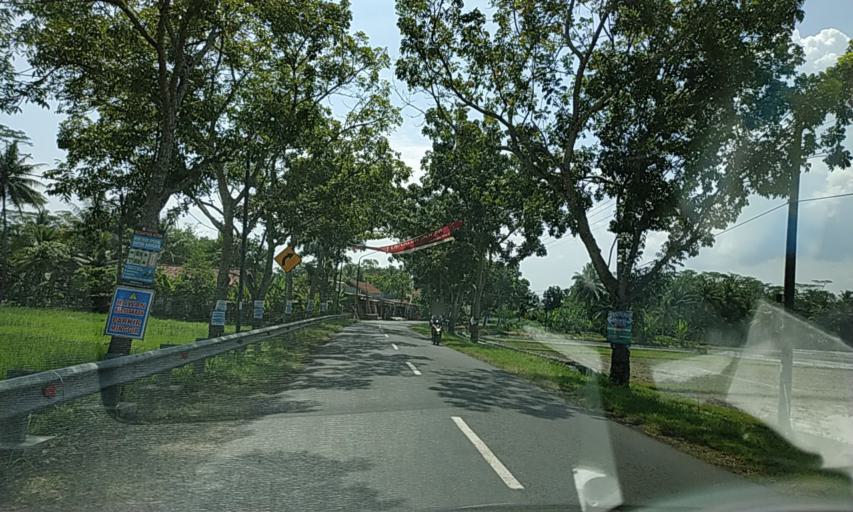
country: ID
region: Central Java
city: Mulyosari
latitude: -7.5185
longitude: 108.7840
